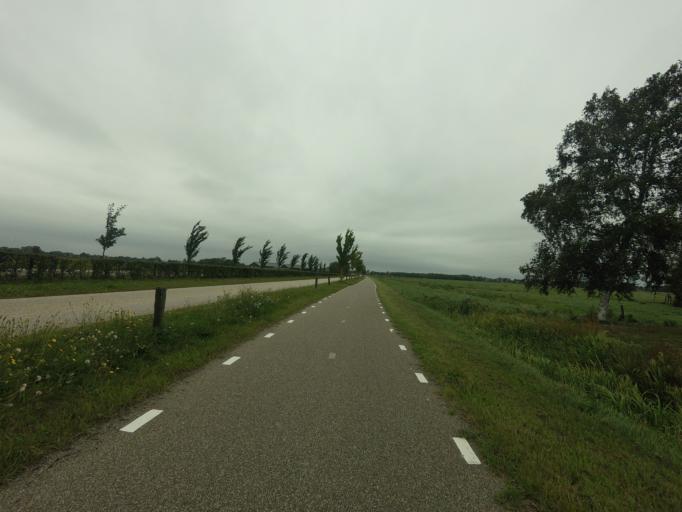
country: NL
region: Friesland
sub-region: Gemeente Opsterland
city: Gorredijk
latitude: 53.0083
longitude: 6.0388
